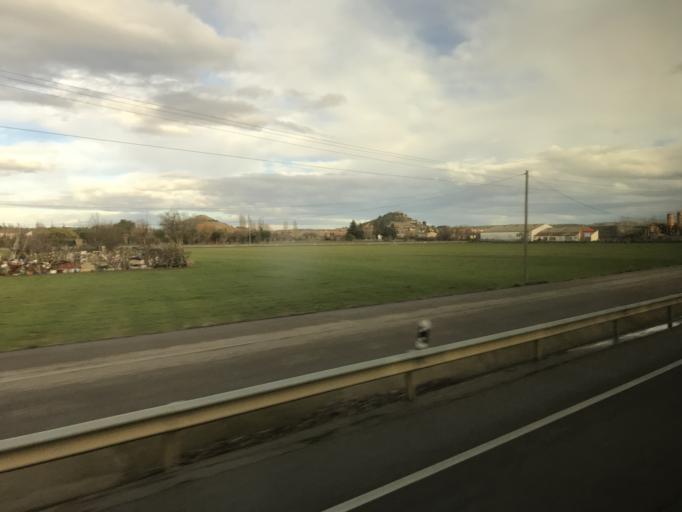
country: ES
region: Castille and Leon
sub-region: Provincia de Palencia
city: Palencia
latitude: 42.0296
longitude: -4.5534
